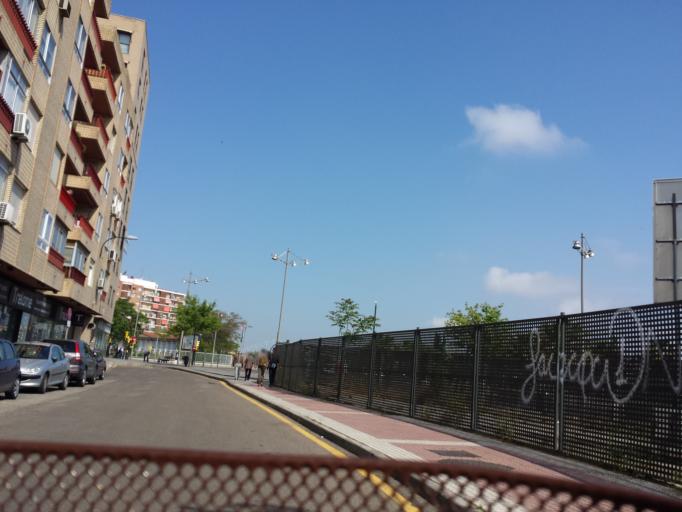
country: ES
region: Aragon
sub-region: Provincia de Zaragoza
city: Almozara
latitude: 41.6545
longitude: -0.8977
